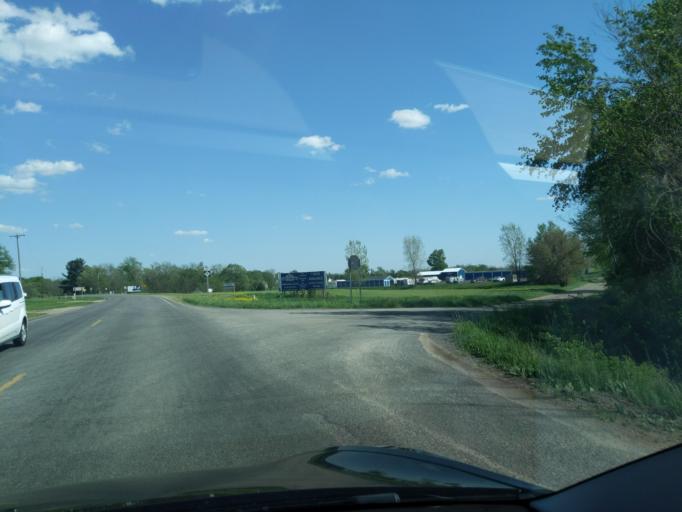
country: US
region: Michigan
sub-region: Ionia County
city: Lake Odessa
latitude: 42.7800
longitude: -85.1532
